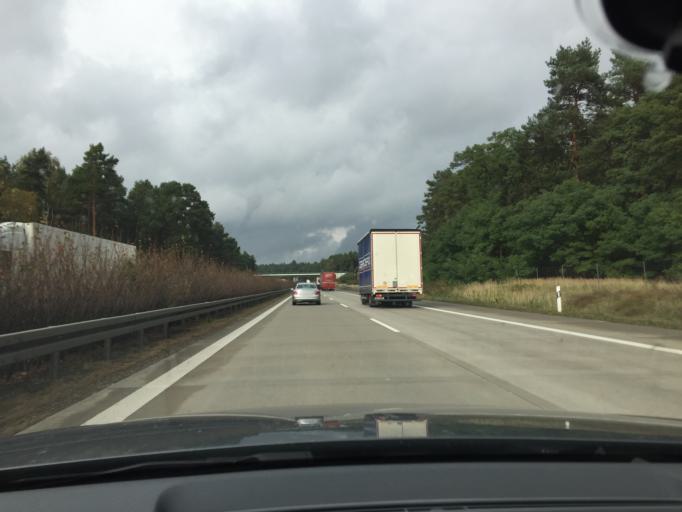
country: DE
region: Brandenburg
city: Schwerin
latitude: 52.1925
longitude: 13.6157
